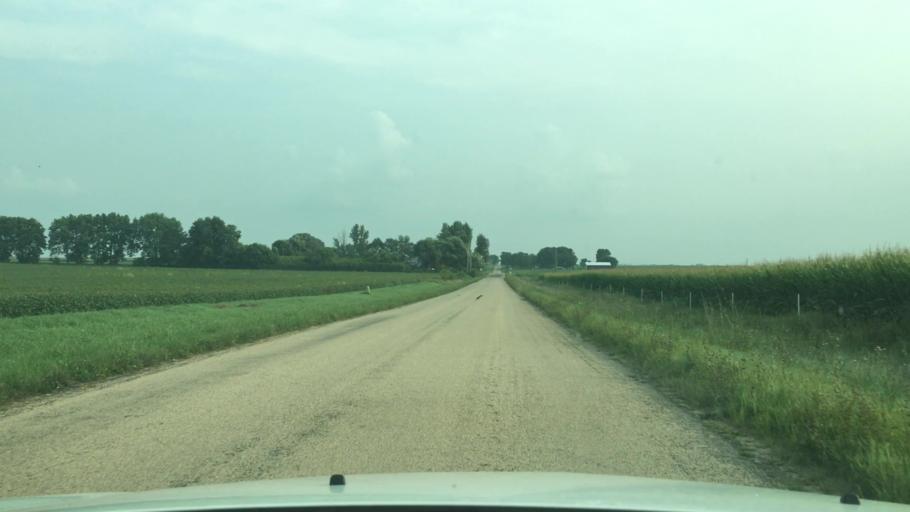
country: US
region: Illinois
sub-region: Ogle County
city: Rochelle
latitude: 41.9230
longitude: -88.9807
